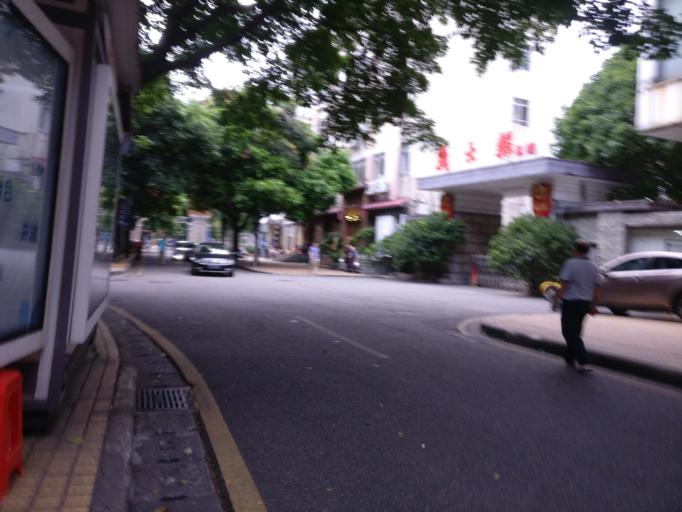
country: CN
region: Guangdong
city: Guangzhou
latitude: 23.1209
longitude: 113.2885
